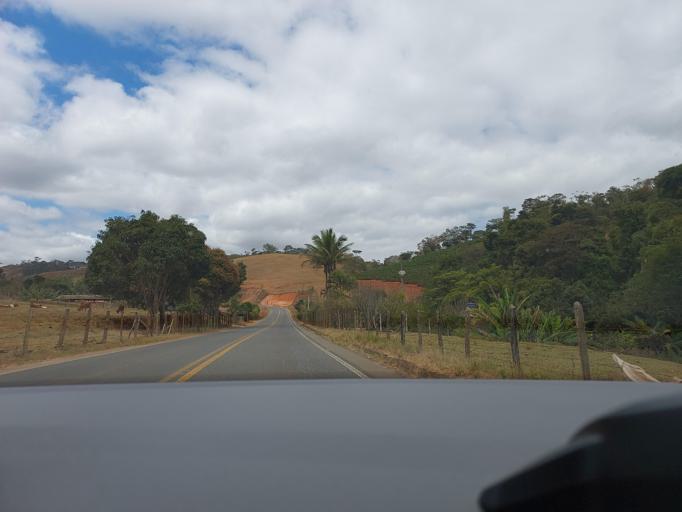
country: BR
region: Minas Gerais
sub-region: Vicosa
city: Vicosa
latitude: -20.8334
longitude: -42.7240
